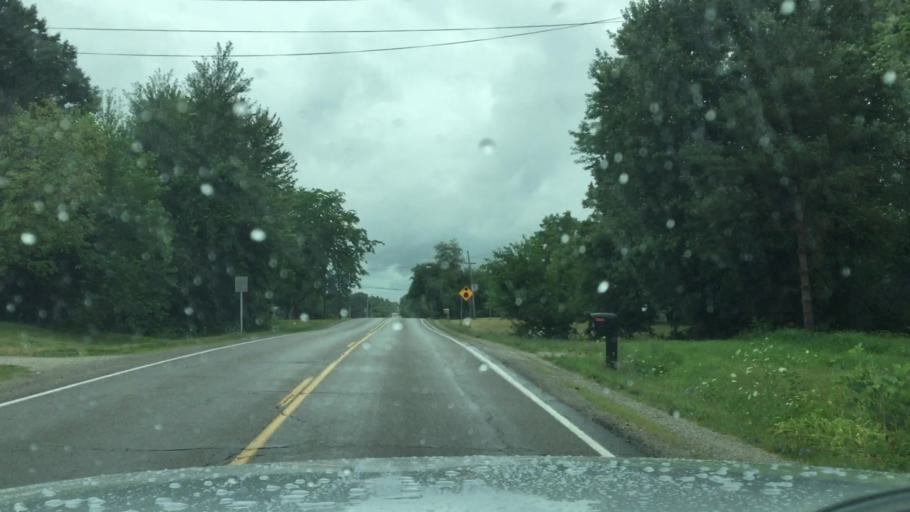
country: US
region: Michigan
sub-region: Genesee County
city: Beecher
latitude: 43.0754
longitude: -83.7496
